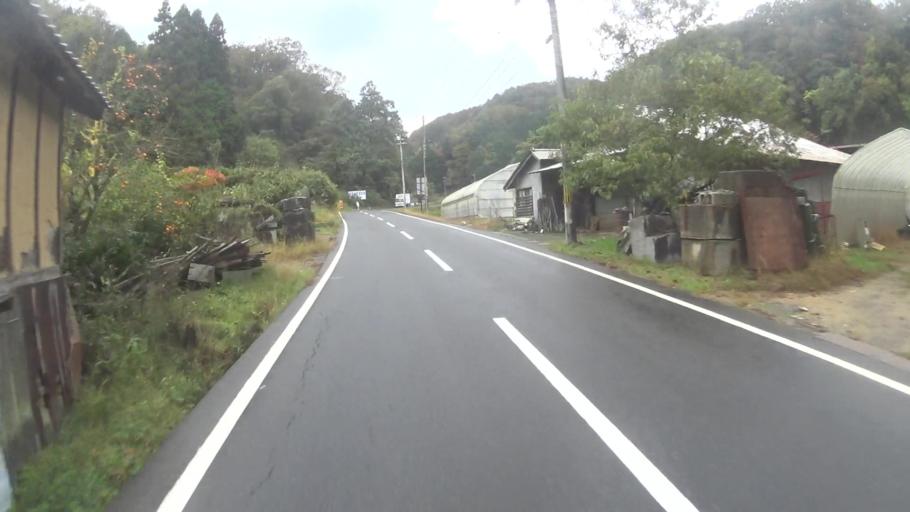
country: JP
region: Kyoto
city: Miyazu
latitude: 35.5254
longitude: 135.0605
